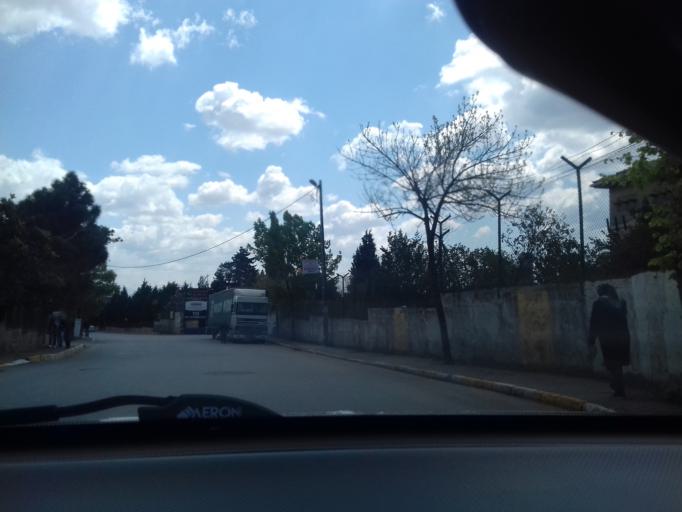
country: TR
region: Istanbul
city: Pendik
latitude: 40.8886
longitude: 29.2802
